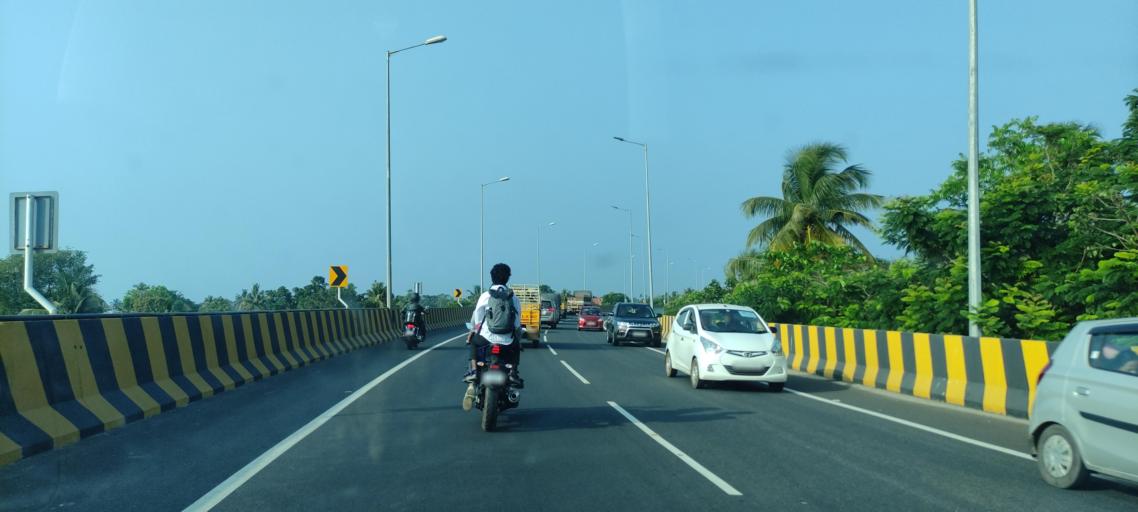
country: IN
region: Kerala
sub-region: Alappuzha
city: Alleppey
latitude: 9.4974
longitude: 76.3177
